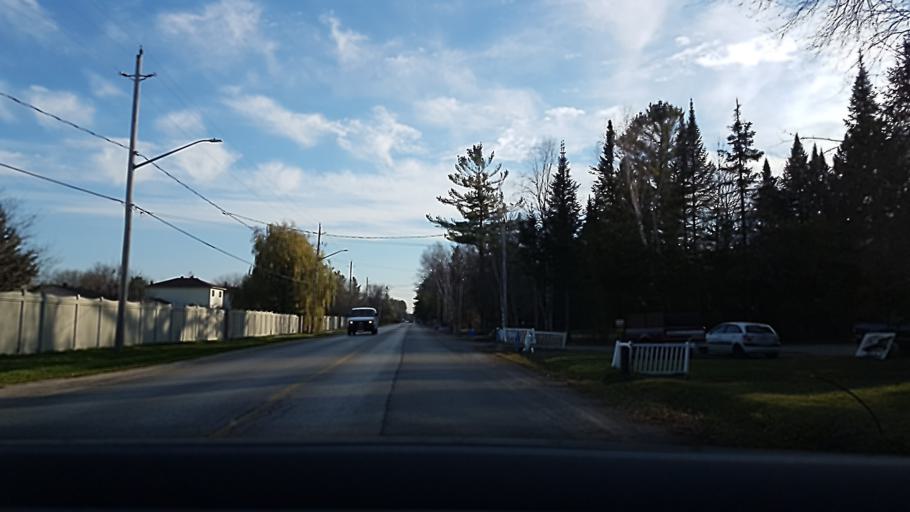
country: CA
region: Ontario
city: Innisfil
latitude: 44.3346
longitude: -79.5444
